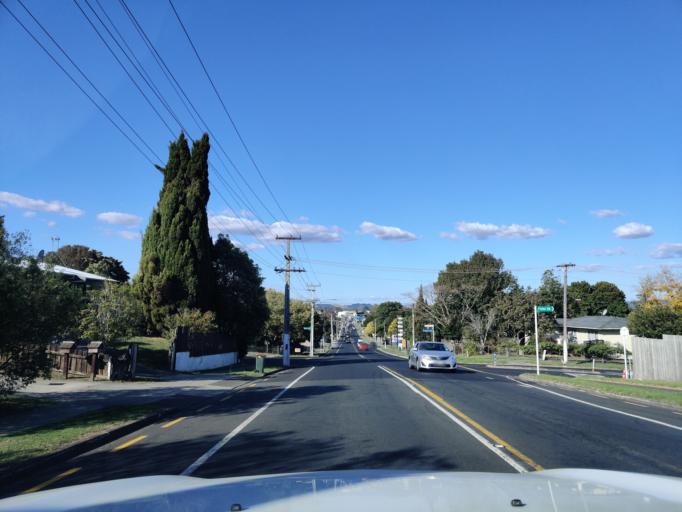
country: NZ
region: Auckland
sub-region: Auckland
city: Takanini
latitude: -37.0352
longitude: 174.8980
